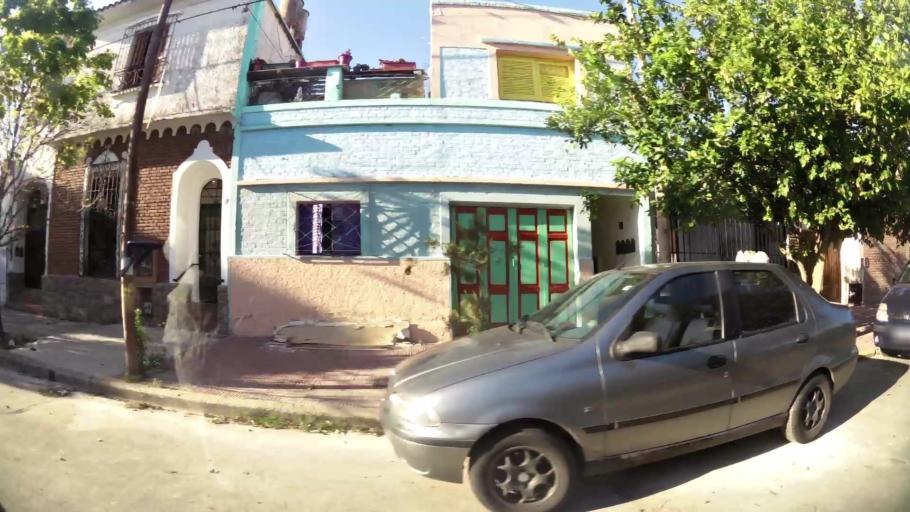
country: AR
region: Cordoba
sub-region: Departamento de Capital
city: Cordoba
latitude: -31.3887
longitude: -64.1860
